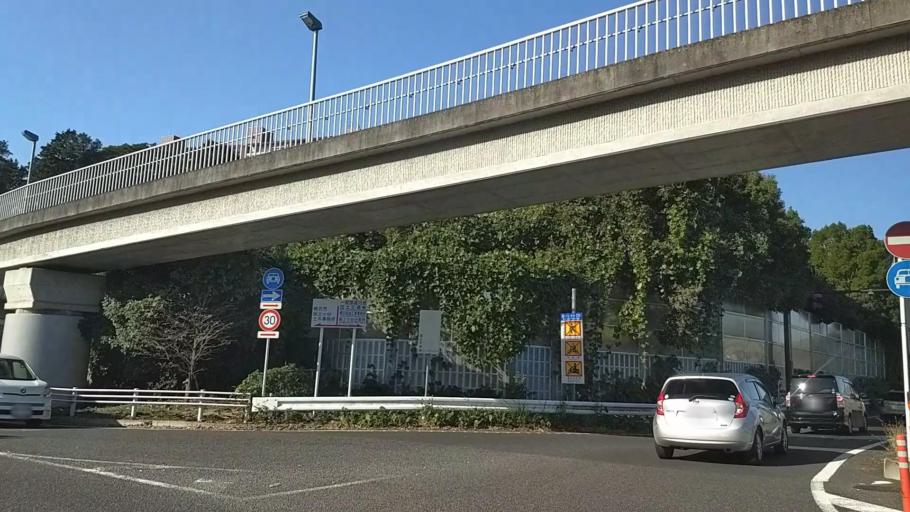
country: JP
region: Kanagawa
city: Yokohama
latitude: 35.4518
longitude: 139.5612
